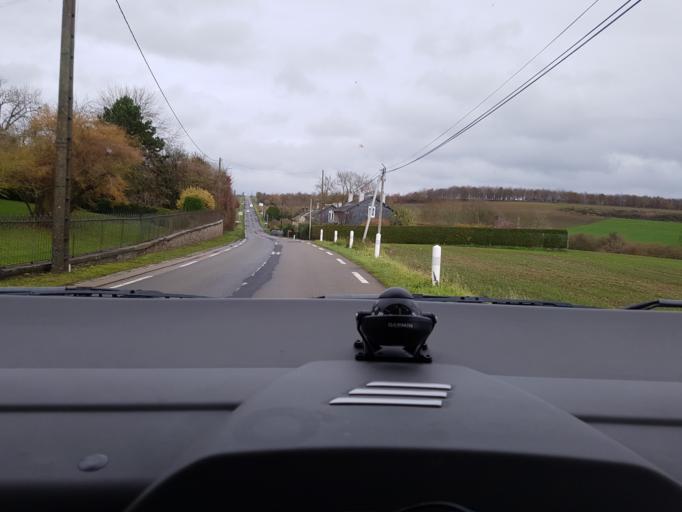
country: FR
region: Haute-Normandie
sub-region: Departement de la Seine-Maritime
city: Gournay-en-Bray
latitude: 49.4877
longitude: 1.7504
